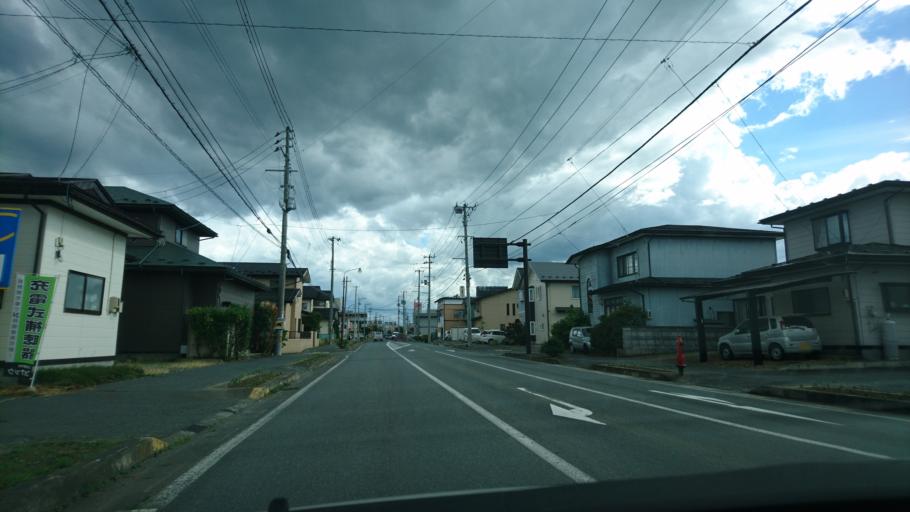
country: JP
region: Iwate
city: Kitakami
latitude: 39.2944
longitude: 141.1208
